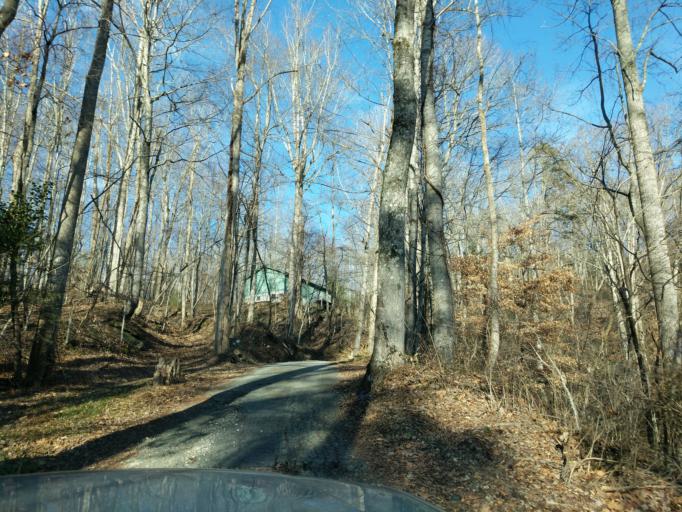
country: US
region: North Carolina
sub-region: Henderson County
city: Edneyville
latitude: 35.4572
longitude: -82.2953
